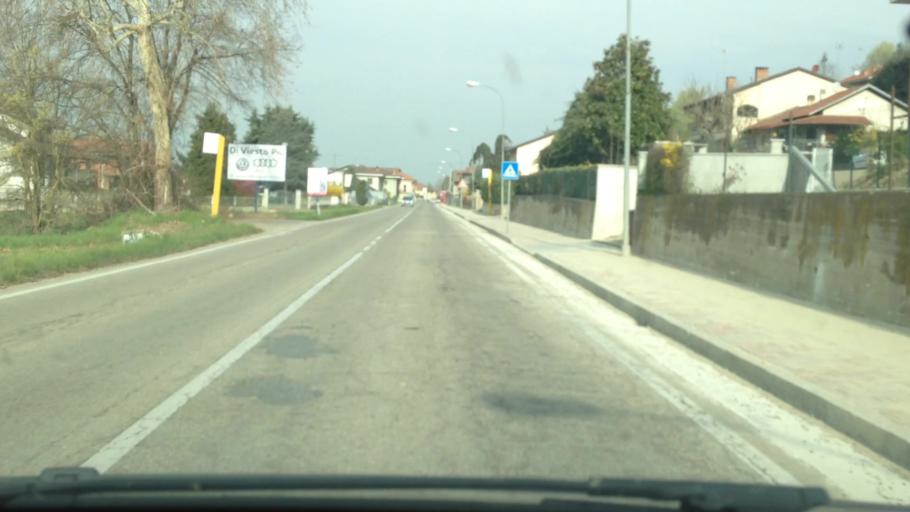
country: IT
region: Piedmont
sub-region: Provincia di Torino
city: Pralormo
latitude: 44.8578
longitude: 7.9037
